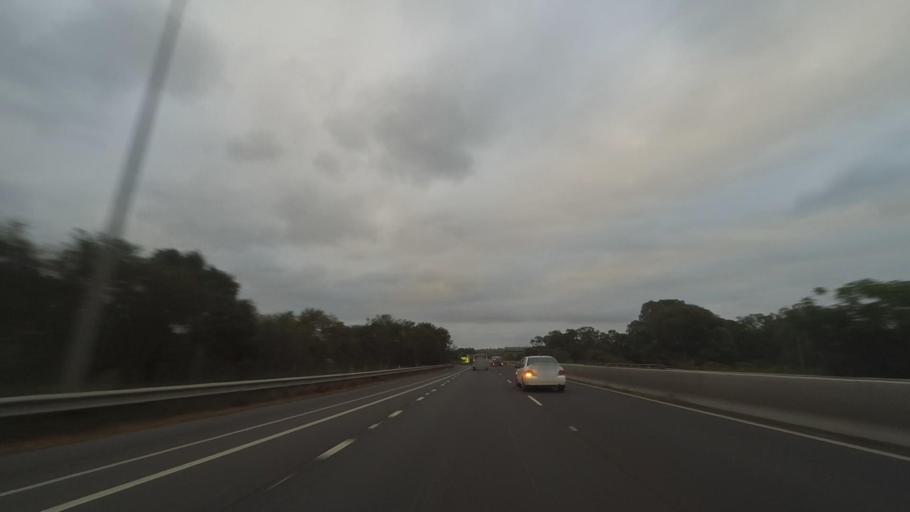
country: AU
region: New South Wales
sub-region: Shellharbour
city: Albion Park Rail
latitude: -34.5381
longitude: 150.7850
